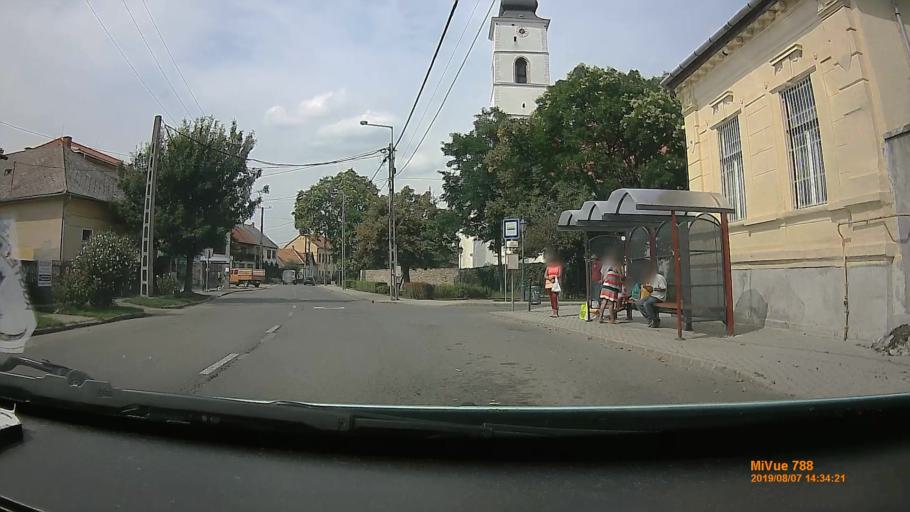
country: HU
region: Borsod-Abauj-Zemplen
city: Szikszo
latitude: 48.2005
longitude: 20.9271
